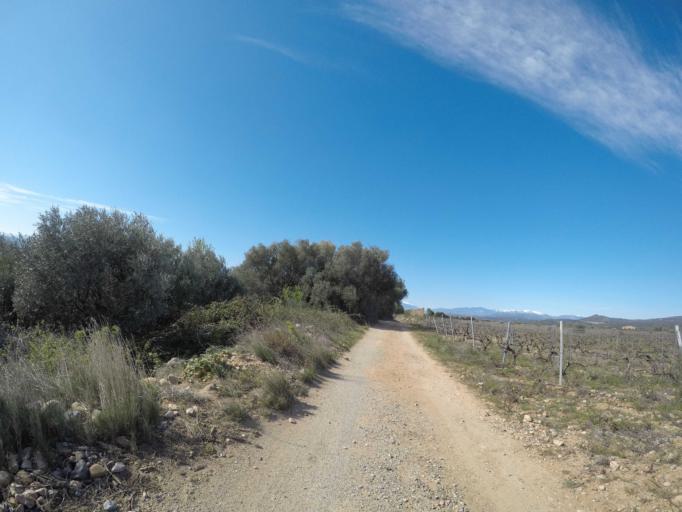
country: FR
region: Languedoc-Roussillon
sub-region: Departement des Pyrenees-Orientales
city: Millas
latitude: 42.7109
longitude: 2.6917
